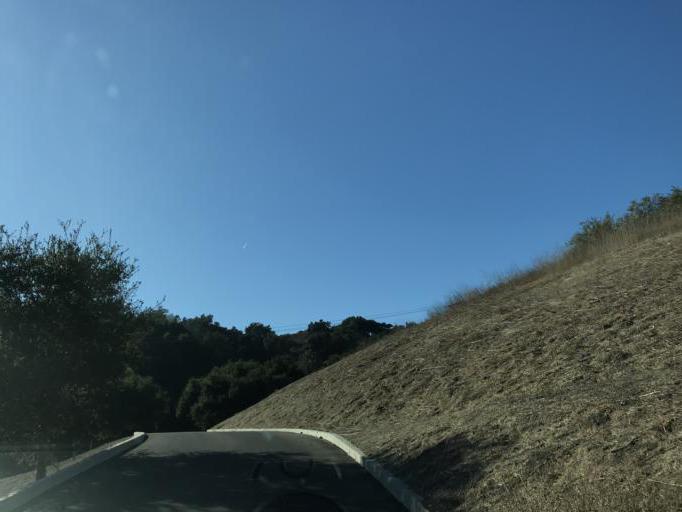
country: US
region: California
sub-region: Santa Barbara County
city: Goleta
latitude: 34.4499
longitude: -119.7771
